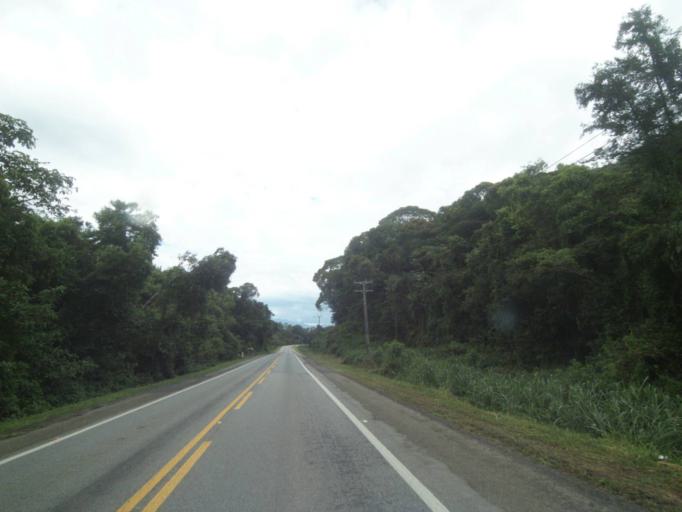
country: BR
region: Parana
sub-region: Antonina
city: Antonina
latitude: -25.4447
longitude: -48.7974
